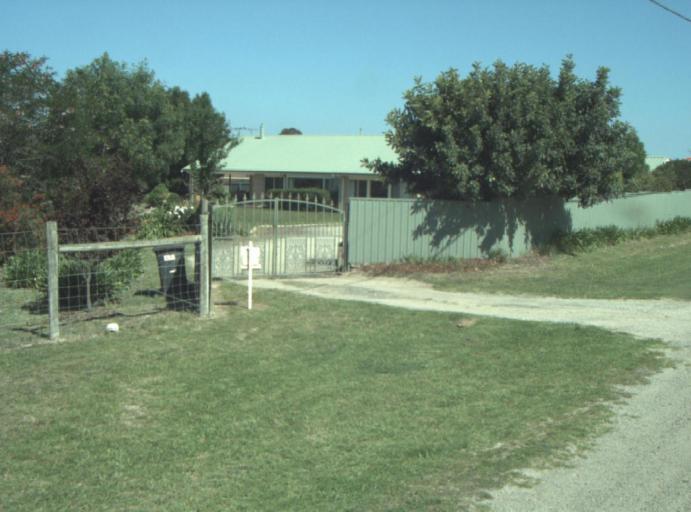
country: AU
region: Victoria
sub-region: Greater Geelong
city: Lara
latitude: -38.0177
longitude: 144.3973
